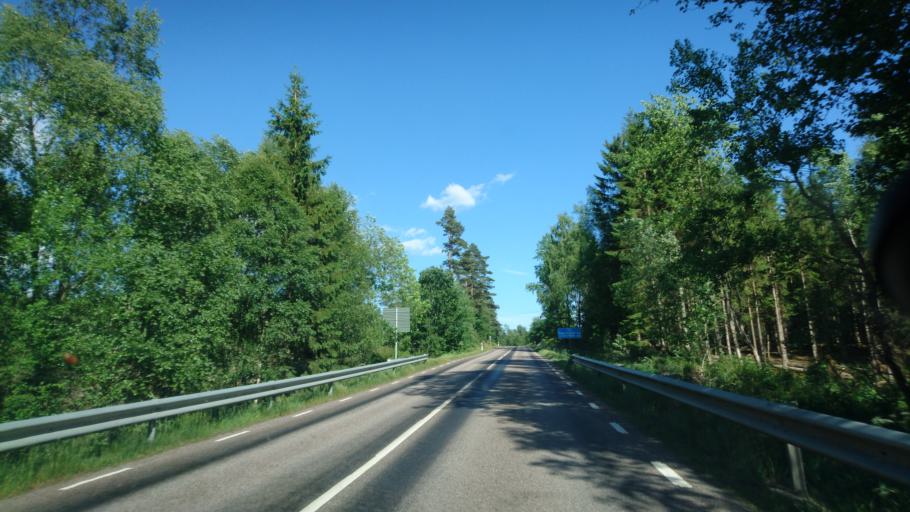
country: SE
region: Skane
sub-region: Osby Kommun
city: Lonsboda
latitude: 56.3919
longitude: 14.3367
